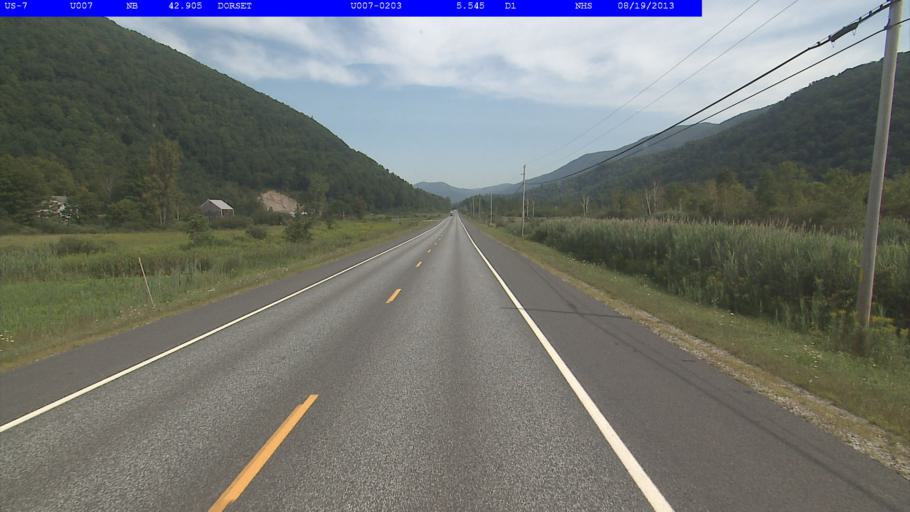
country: US
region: Vermont
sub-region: Bennington County
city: Manchester Center
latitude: 43.2884
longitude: -73.0004
